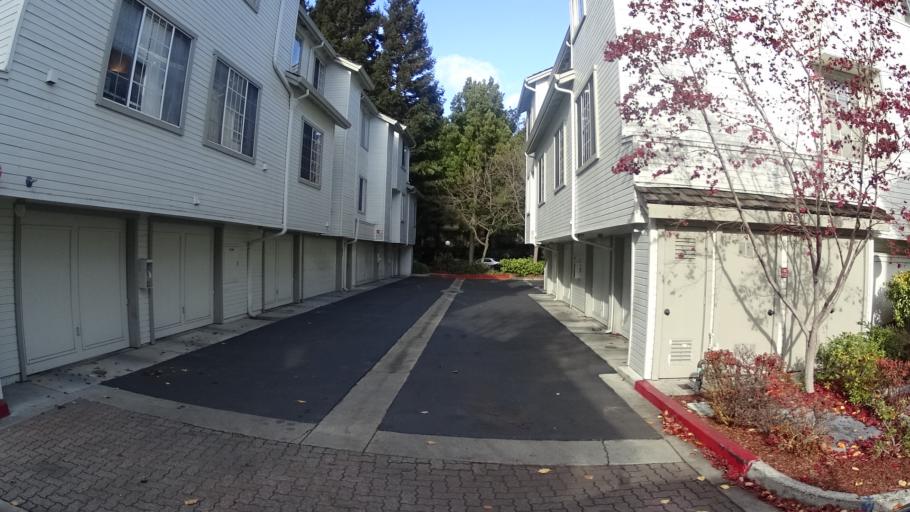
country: US
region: California
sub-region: Santa Clara County
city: Sunnyvale
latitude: 37.3841
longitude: -122.0421
